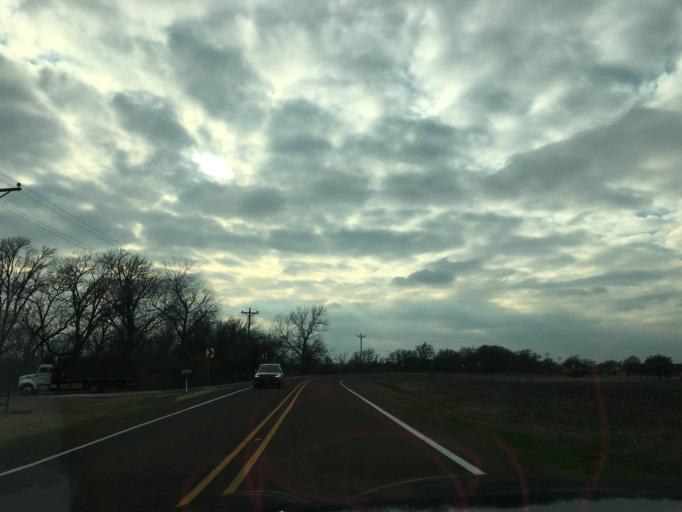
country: US
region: Texas
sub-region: Ellis County
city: Palmer
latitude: 32.4487
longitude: -96.7103
